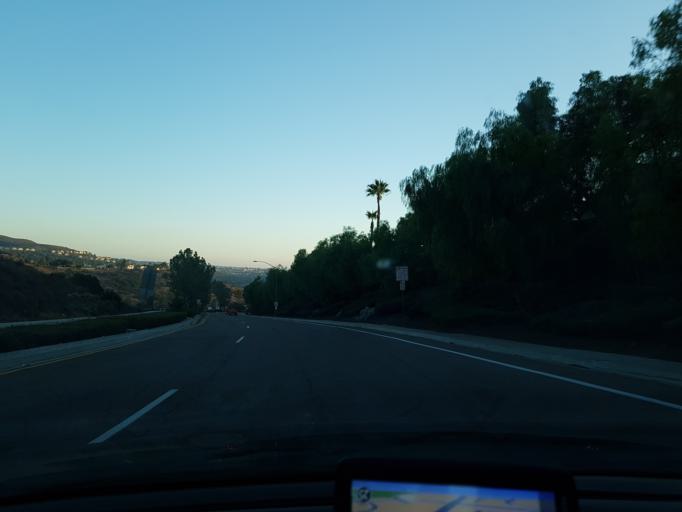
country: US
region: California
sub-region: San Diego County
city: Fairbanks Ranch
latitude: 32.9513
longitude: -117.1305
